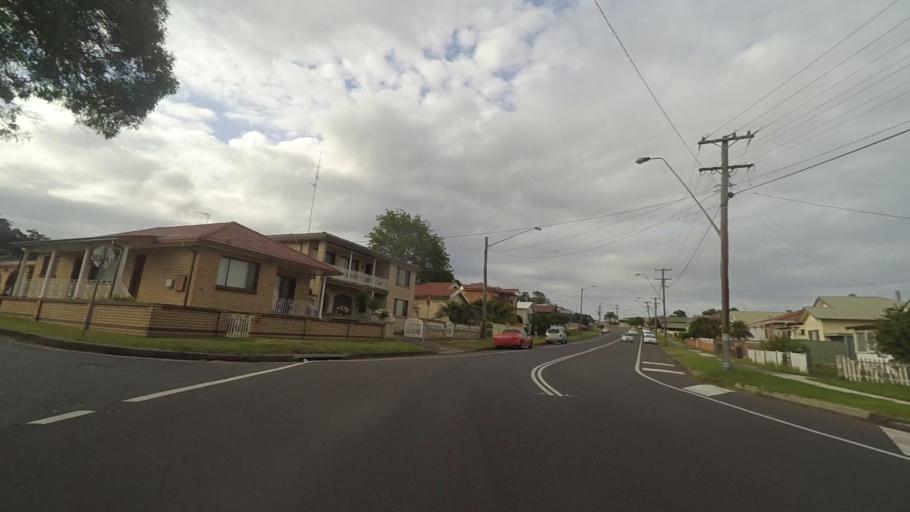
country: AU
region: New South Wales
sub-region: Wollongong
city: Wollongong
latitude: -34.4339
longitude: 150.8859
